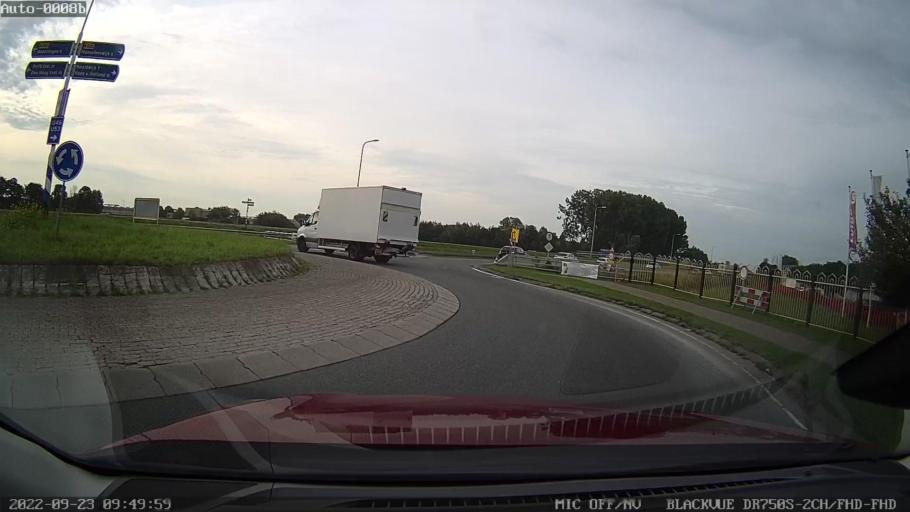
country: NL
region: South Holland
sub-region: Gemeente Westland
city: Kwintsheul
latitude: 51.9955
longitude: 4.2594
